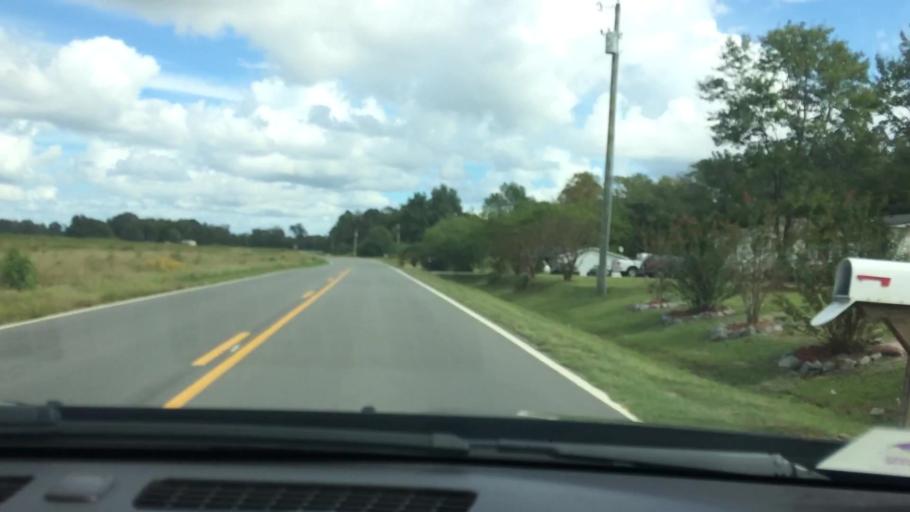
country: US
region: North Carolina
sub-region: Pitt County
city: Ayden
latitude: 35.4565
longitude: -77.4757
